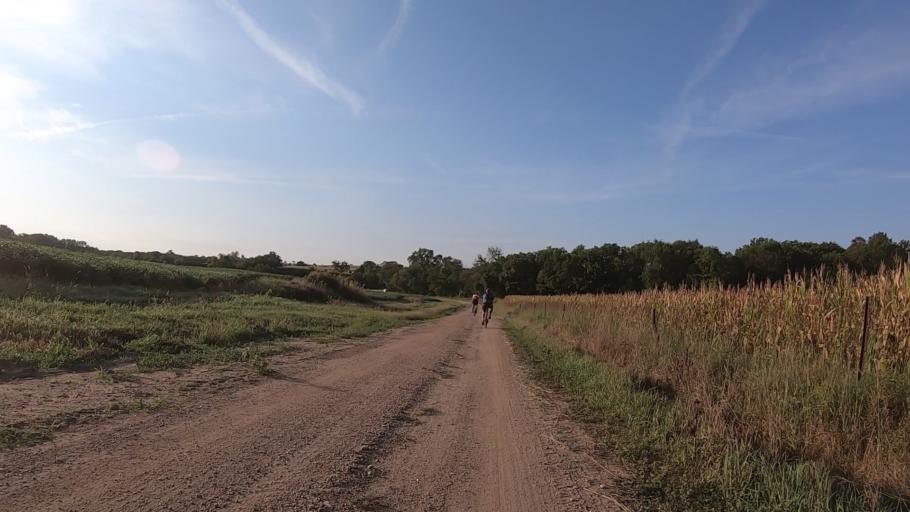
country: US
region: Kansas
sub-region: Marshall County
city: Blue Rapids
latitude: 39.7230
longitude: -96.8070
